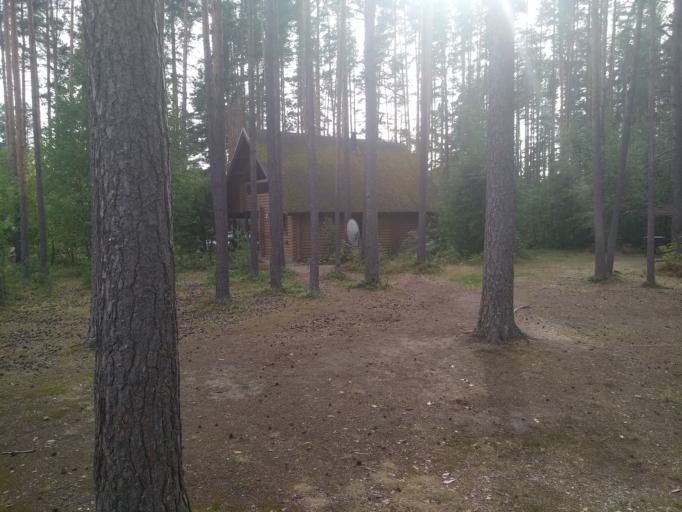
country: RU
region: Leningrad
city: Sapernoye
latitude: 60.6821
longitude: 30.0535
